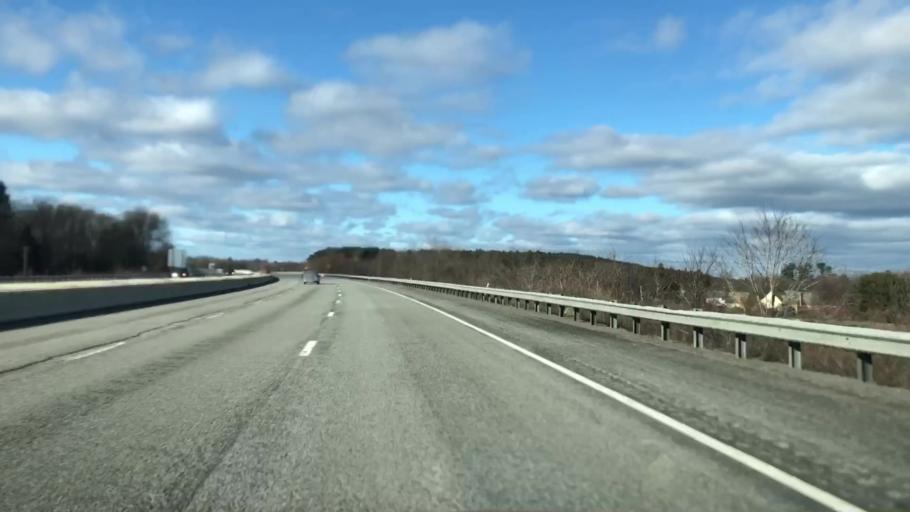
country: US
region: Massachusetts
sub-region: Worcester County
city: West Boylston
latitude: 42.3416
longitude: -71.8003
